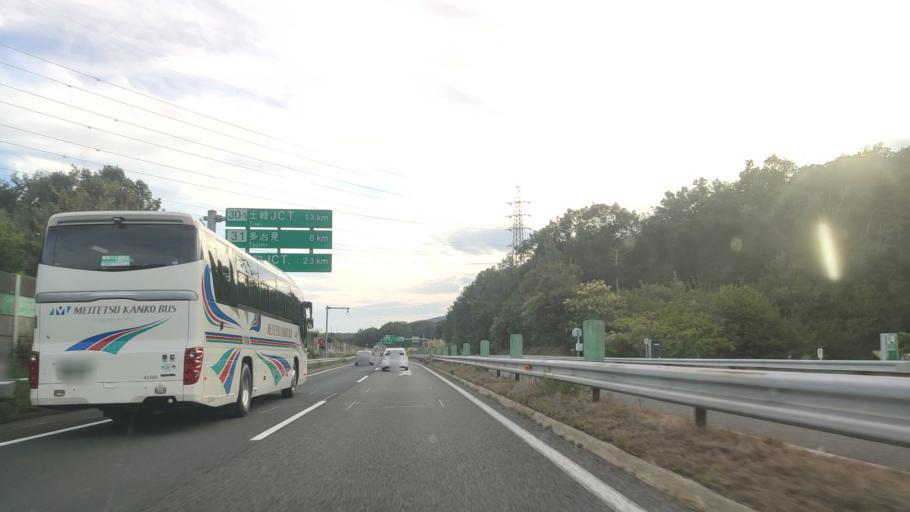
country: JP
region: Gifu
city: Toki
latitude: 35.3726
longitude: 137.1846
